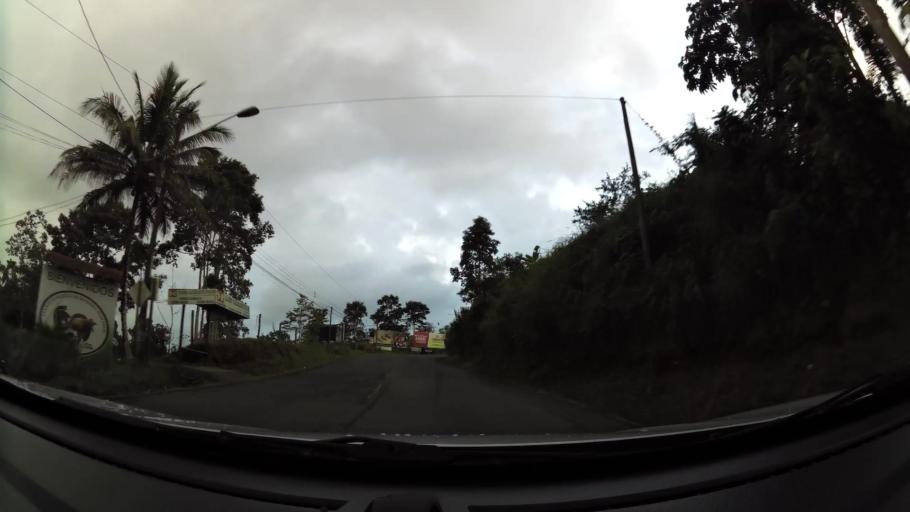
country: CR
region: Cartago
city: Turrialba
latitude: 9.8968
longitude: -83.6883
